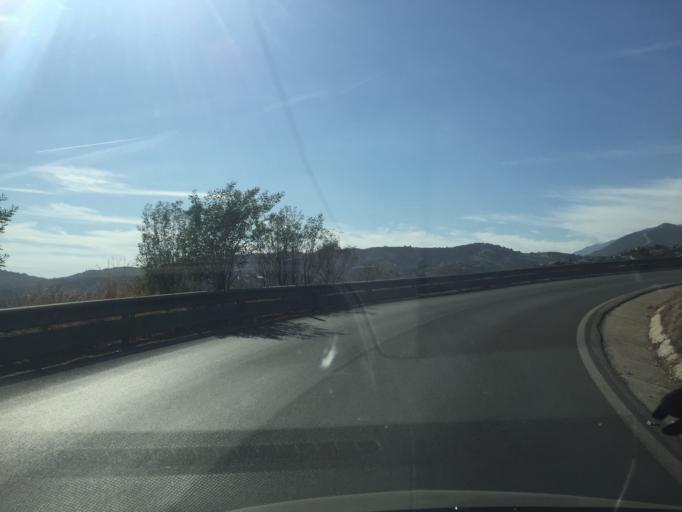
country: ES
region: Andalusia
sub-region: Provincia de Malaga
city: Frigiliana
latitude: 36.7794
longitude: -3.8982
